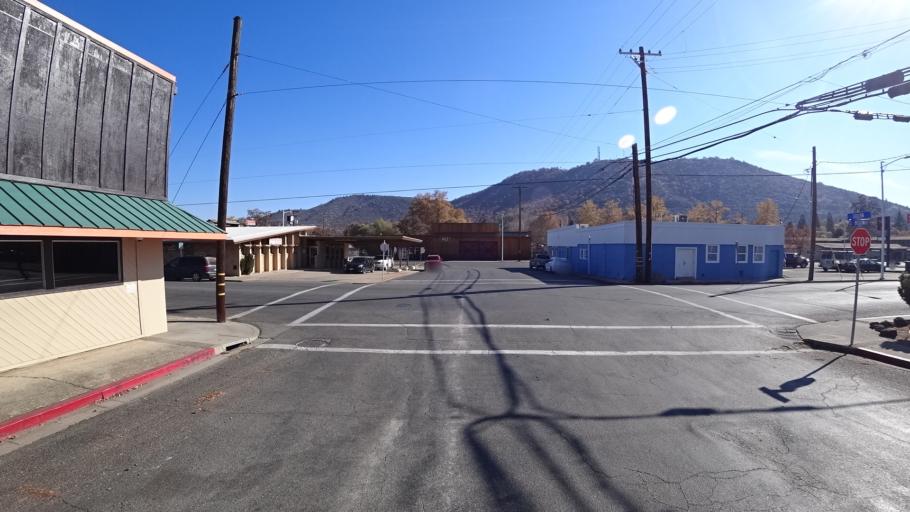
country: US
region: California
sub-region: Siskiyou County
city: Yreka
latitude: 41.7286
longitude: -122.6376
